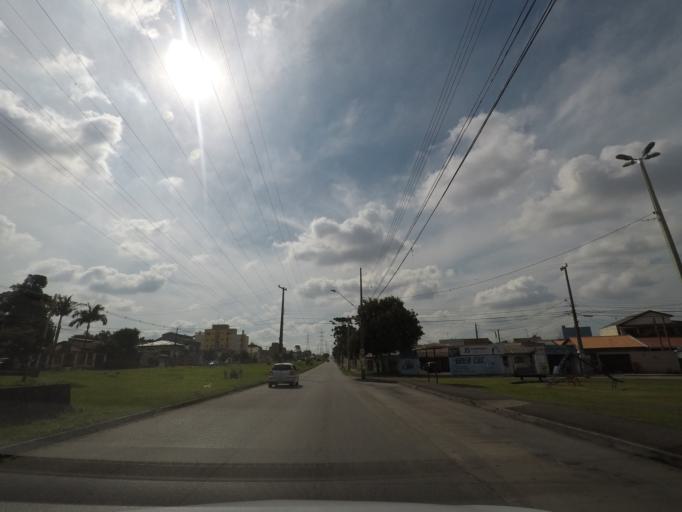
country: BR
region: Parana
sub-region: Sao Jose Dos Pinhais
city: Sao Jose dos Pinhais
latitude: -25.4877
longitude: -49.2070
